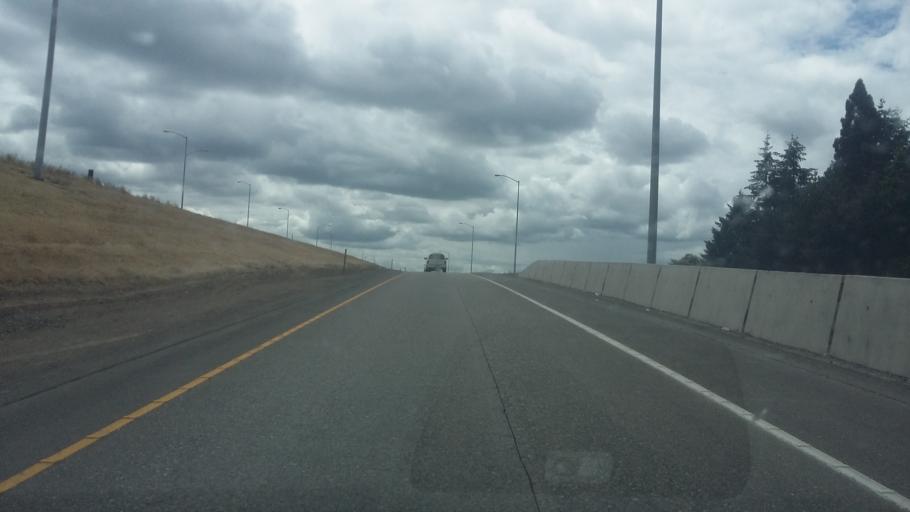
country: US
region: Oregon
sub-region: Multnomah County
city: Lents
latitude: 45.5020
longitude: -122.5664
